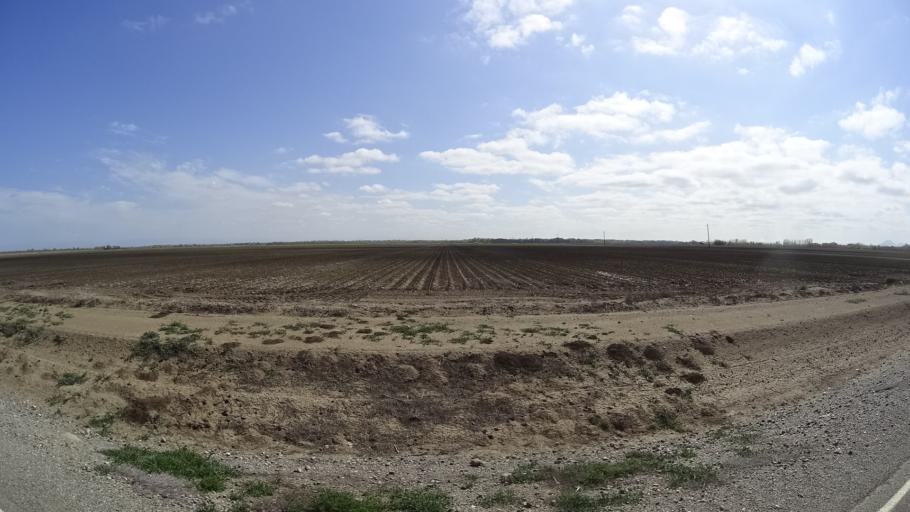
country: US
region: California
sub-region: Butte County
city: Biggs
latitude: 39.4358
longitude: -121.9298
